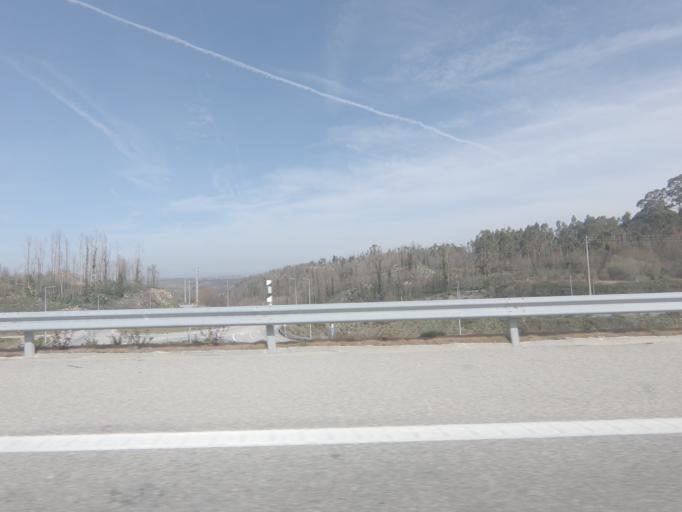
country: PT
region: Viseu
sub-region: Vouzela
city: Vouzela
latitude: 40.6503
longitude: -8.0708
